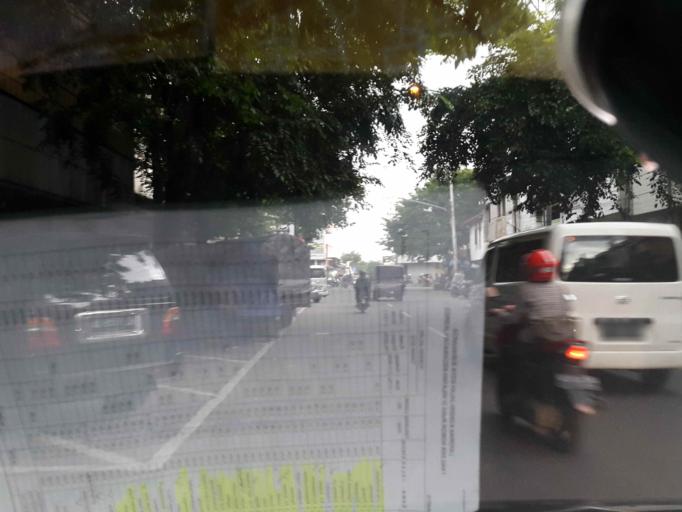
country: ID
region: Central Java
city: Surakarta
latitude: -7.5637
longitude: 110.8244
